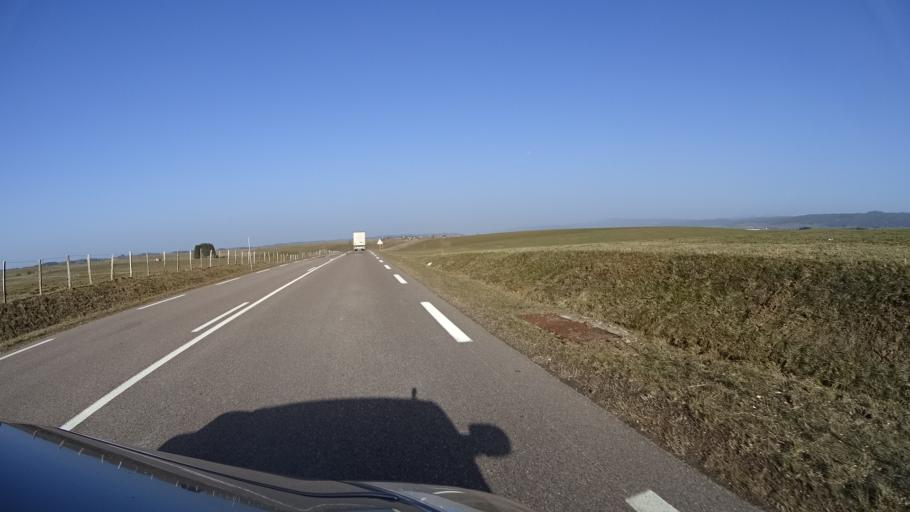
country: FR
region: Franche-Comte
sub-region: Departement du Doubs
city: Frasne
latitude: 46.8817
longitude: 6.2006
